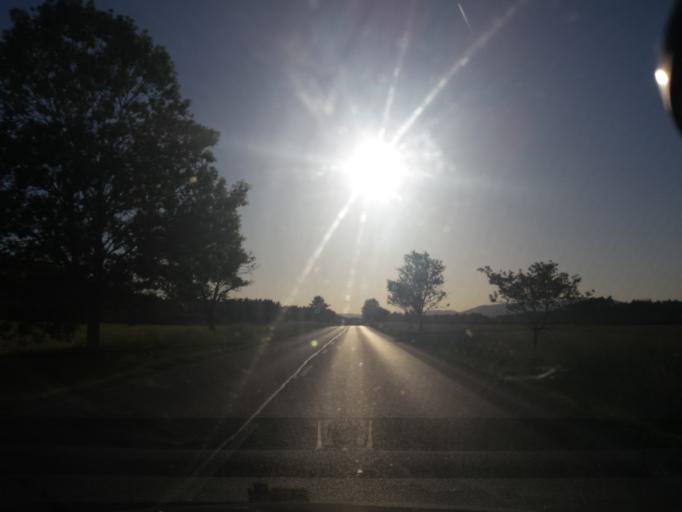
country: CZ
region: Liberecky
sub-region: Okres Ceska Lipa
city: Ceska Lipa
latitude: 50.6146
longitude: 14.5659
